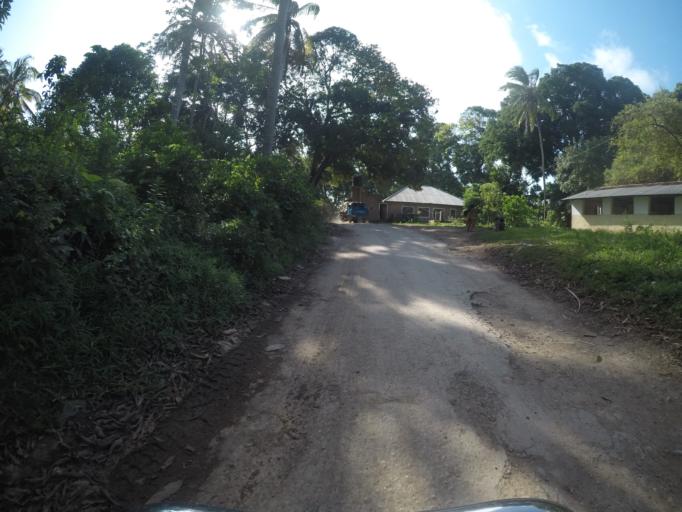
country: TZ
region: Zanzibar Central/South
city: Koani
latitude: -6.2184
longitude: 39.3247
